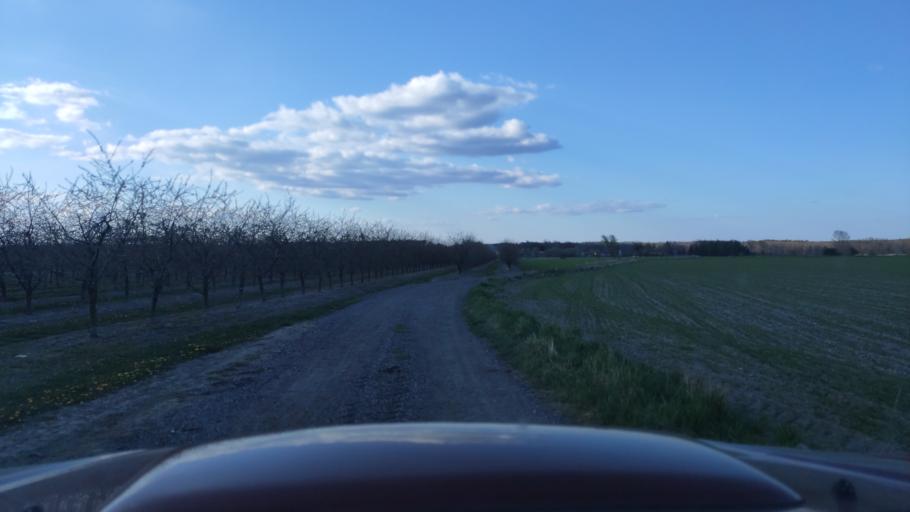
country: PL
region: Masovian Voivodeship
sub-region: Powiat zwolenski
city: Zwolen
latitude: 51.3776
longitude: 21.5751
